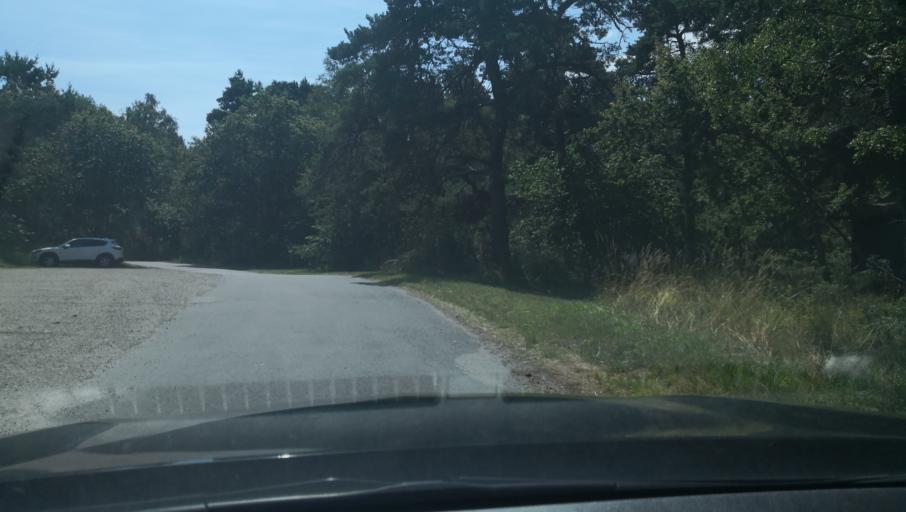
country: SE
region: Skane
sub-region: Ystads Kommun
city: Kopingebro
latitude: 55.3870
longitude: 14.1463
